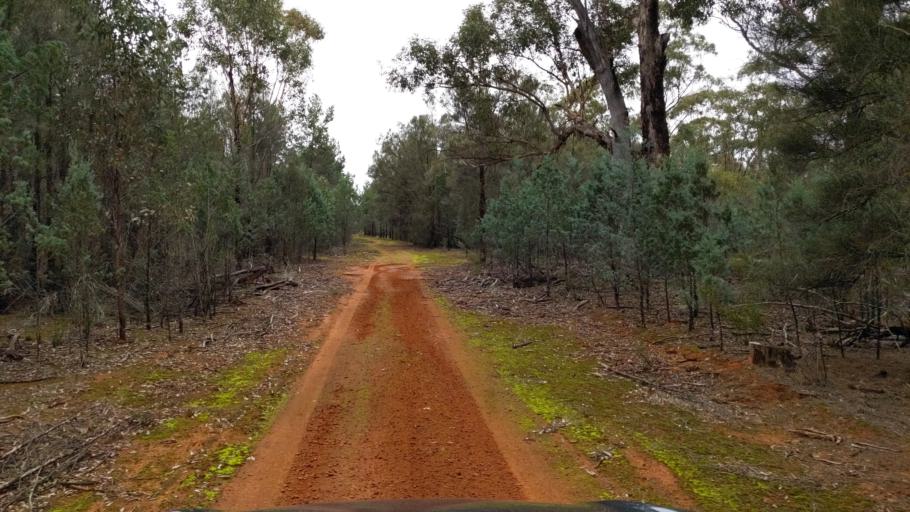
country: AU
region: New South Wales
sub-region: Coolamon
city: Coolamon
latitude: -34.8296
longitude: 146.9357
